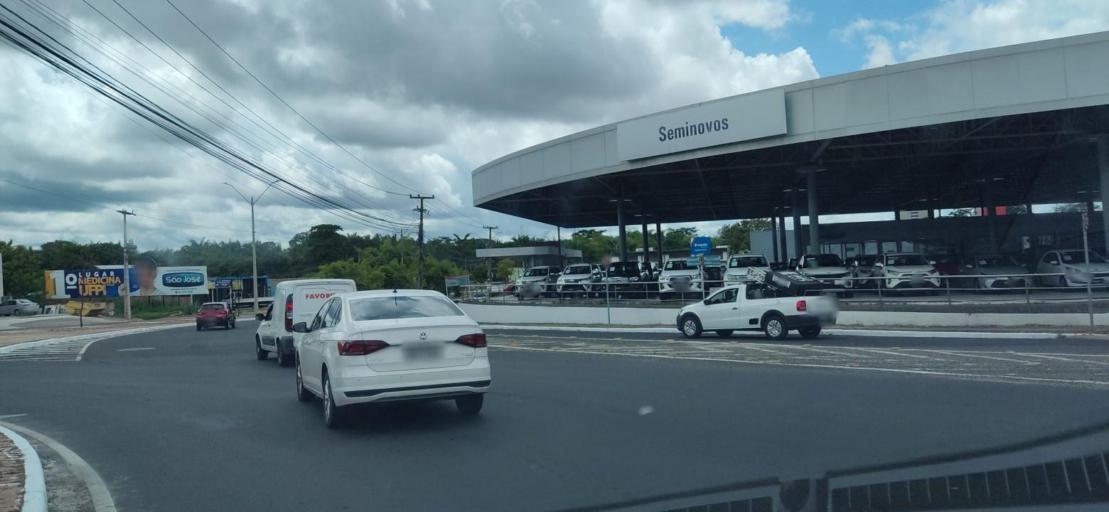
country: BR
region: Piaui
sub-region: Teresina
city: Teresina
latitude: -5.0626
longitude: -42.8042
